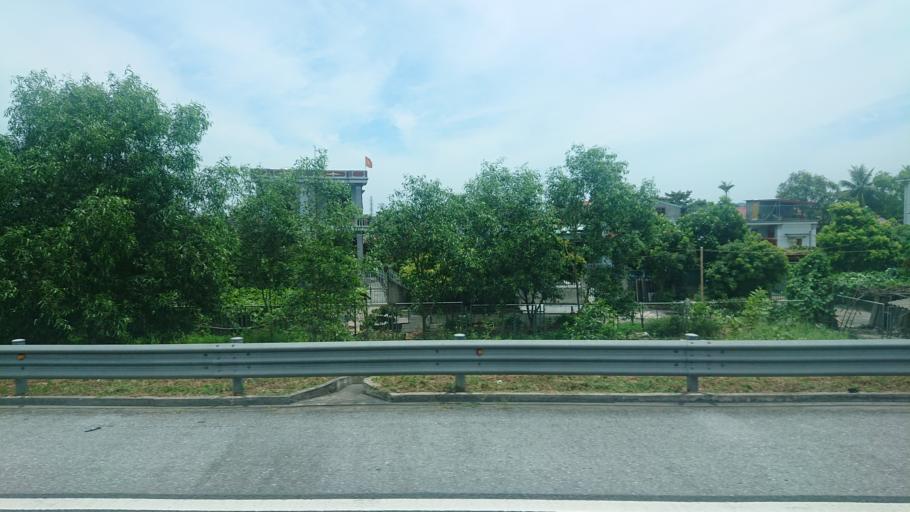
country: VN
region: Hai Phong
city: An Lao
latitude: 20.8011
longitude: 106.5315
